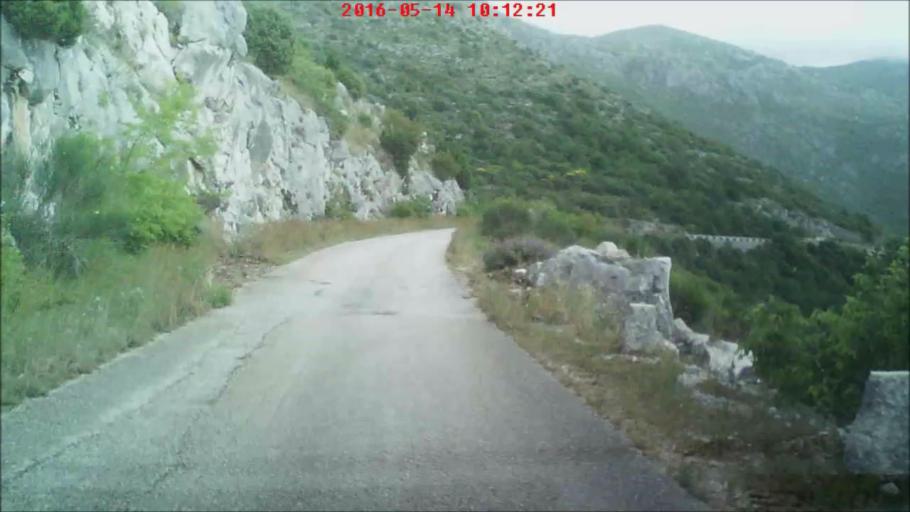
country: HR
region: Dubrovacko-Neretvanska
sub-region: Grad Dubrovnik
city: Mokosica
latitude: 42.7352
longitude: 17.9480
